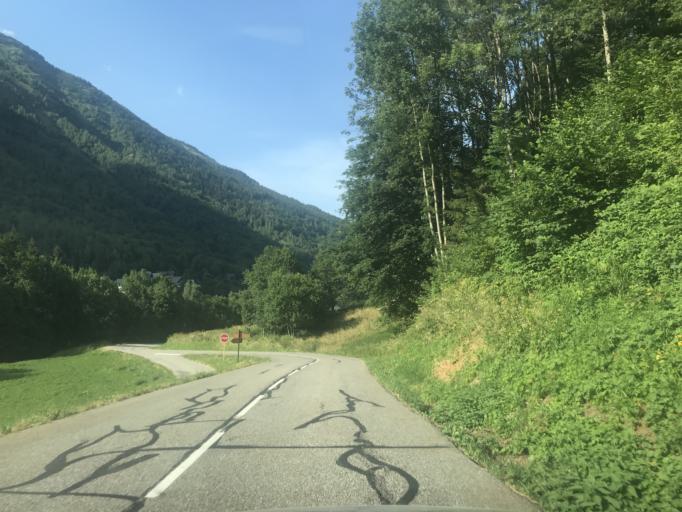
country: FR
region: Rhone-Alpes
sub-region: Departement de la Savoie
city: Saint-Etienne-de-Cuines
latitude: 45.2860
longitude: 6.2161
